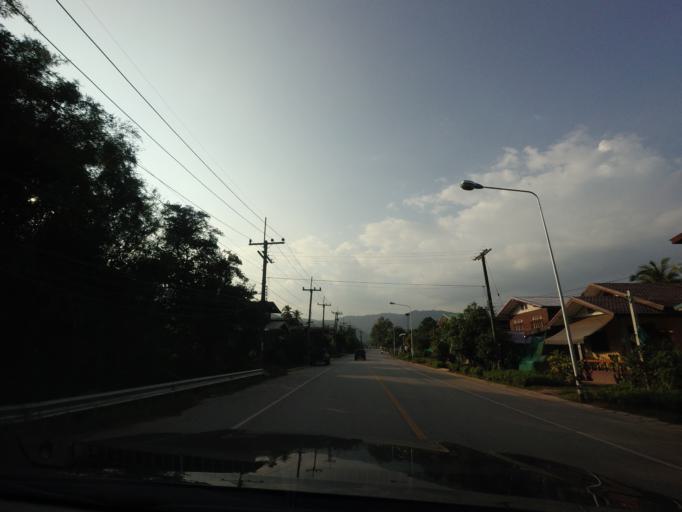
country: TH
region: Loei
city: Dan Sai
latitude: 17.2884
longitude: 101.1340
